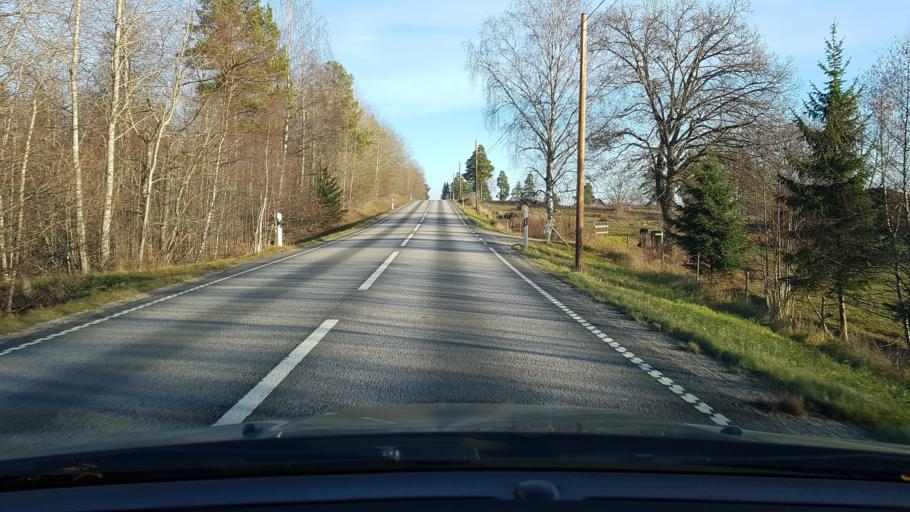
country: SE
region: Stockholm
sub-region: Norrtalje Kommun
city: Nykvarn
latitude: 59.7375
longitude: 18.2932
